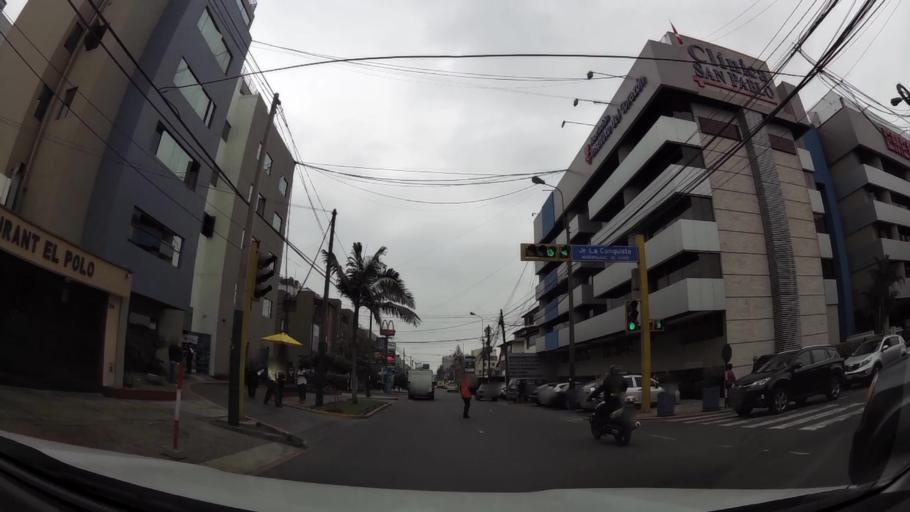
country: PE
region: Lima
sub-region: Lima
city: La Molina
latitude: -12.1001
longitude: -76.9711
